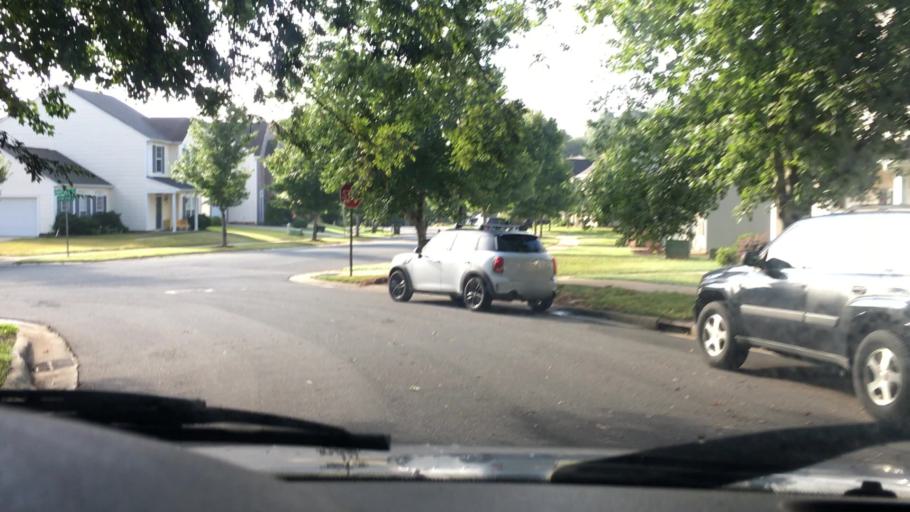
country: US
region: North Carolina
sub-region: Mecklenburg County
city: Huntersville
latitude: 35.3819
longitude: -80.9171
